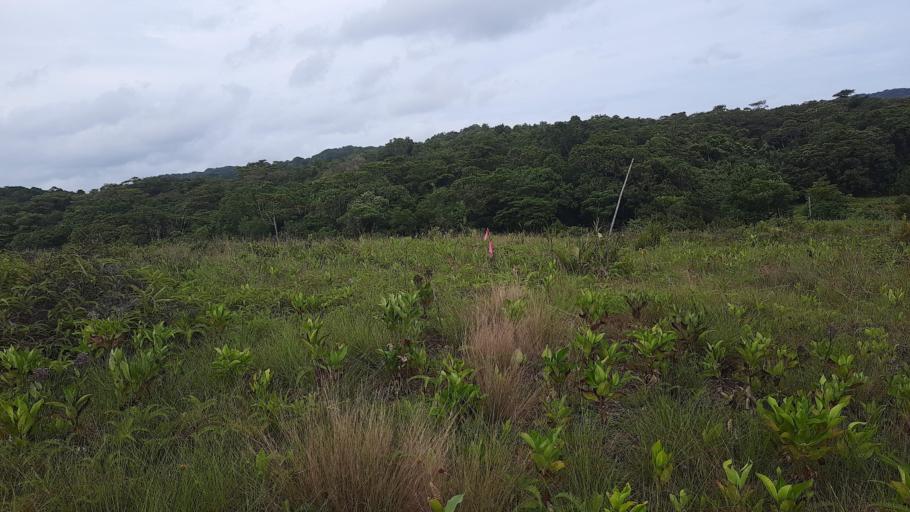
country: PW
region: Aimeliik
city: Ngchemiangel
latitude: 7.4471
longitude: 134.5377
